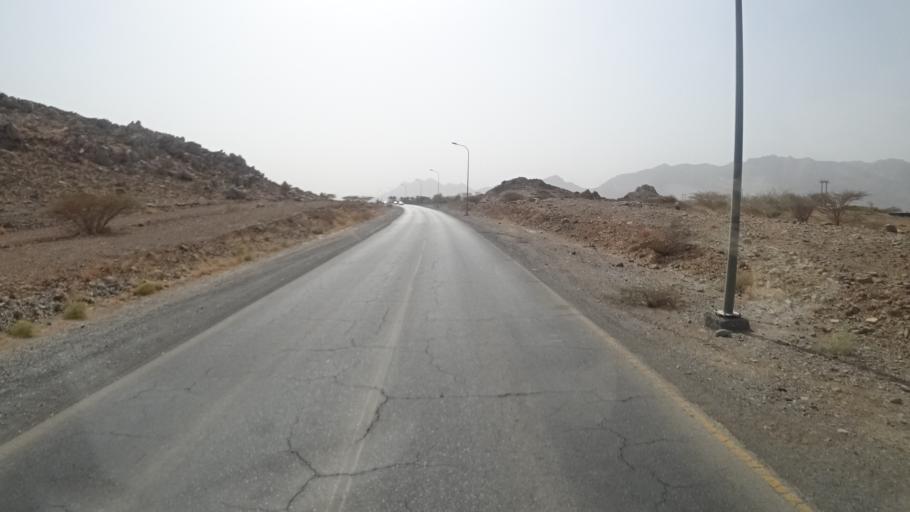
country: OM
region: Muhafazat ad Dakhiliyah
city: Nizwa
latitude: 22.9254
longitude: 57.6236
